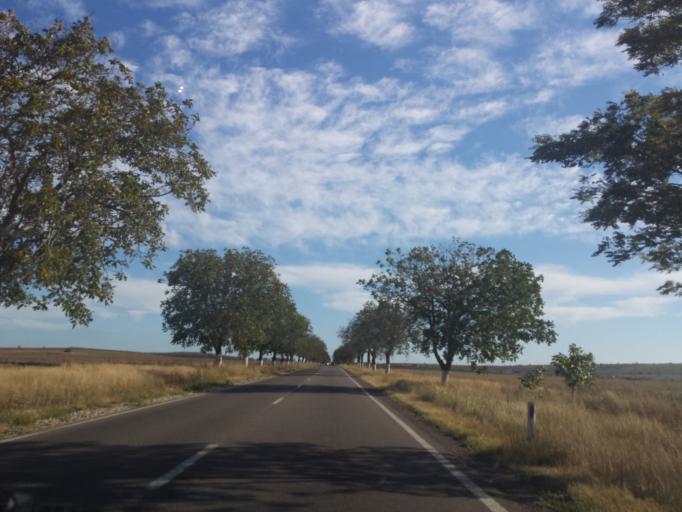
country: RO
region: Tulcea
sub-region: Comuna Frecatei
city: Cataloi
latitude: 45.1182
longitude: 28.7495
